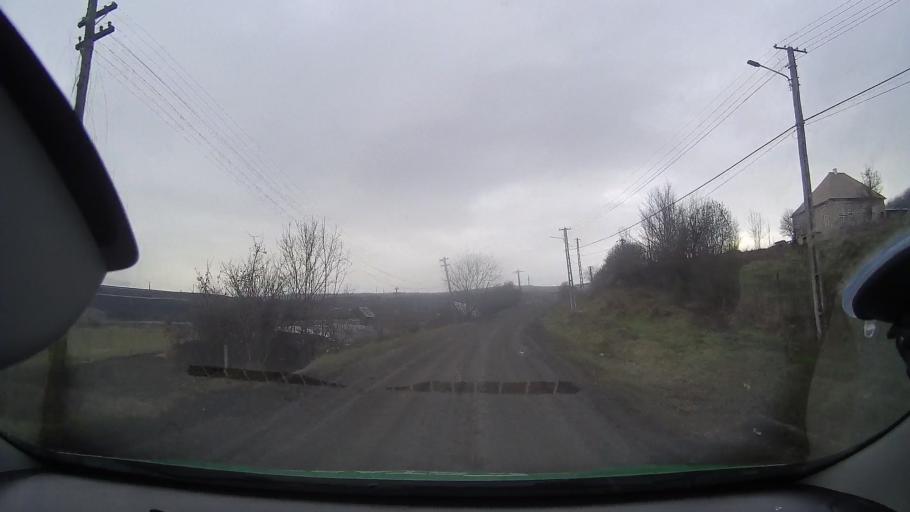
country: RO
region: Mures
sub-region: Comuna Bichis
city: Bichis
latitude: 46.3756
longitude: 24.0836
